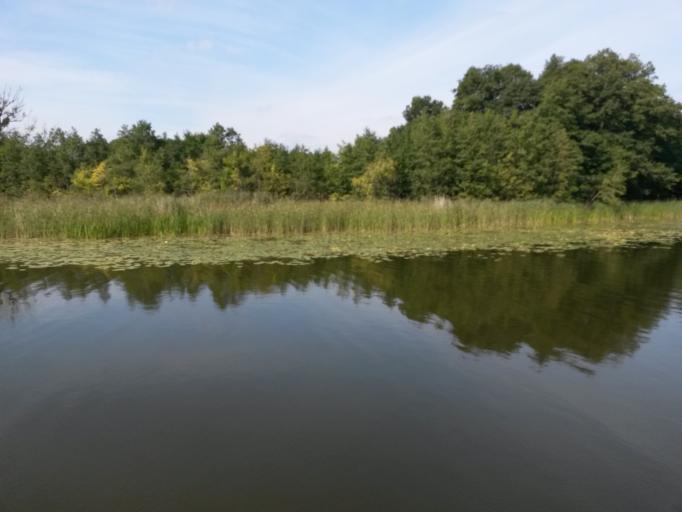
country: DE
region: Brandenburg
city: Templin
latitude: 53.1364
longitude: 13.5436
